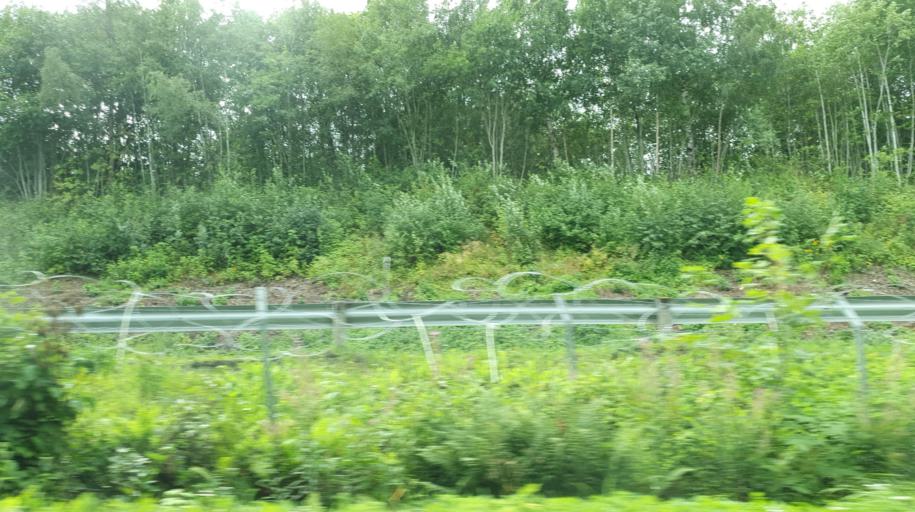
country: NO
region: Nord-Trondelag
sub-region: Stjordal
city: Stjordalshalsen
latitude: 63.4565
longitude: 10.9515
